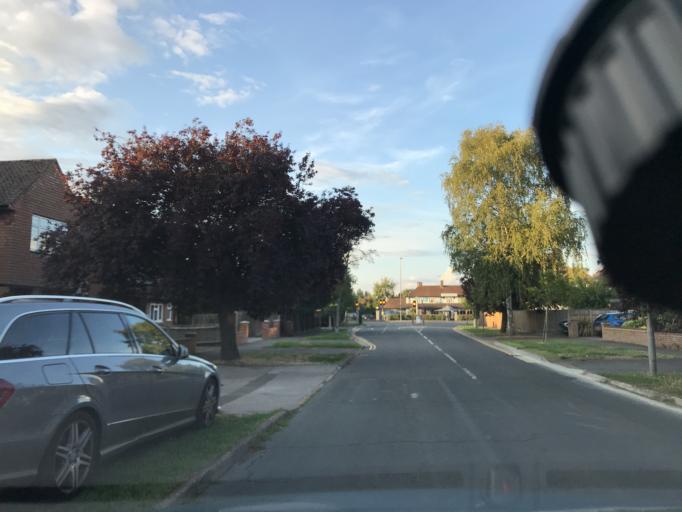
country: GB
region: England
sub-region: Buckinghamshire
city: Aylesbury
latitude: 51.8140
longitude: -0.7907
